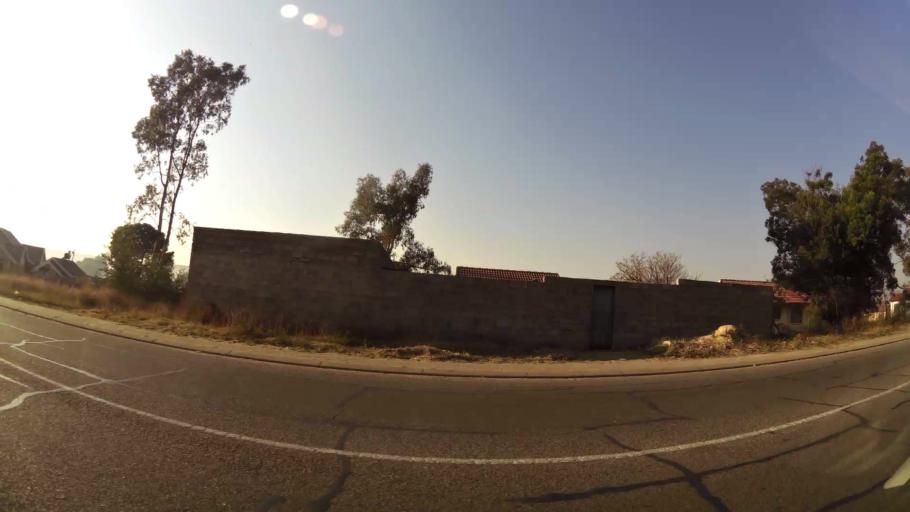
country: ZA
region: Gauteng
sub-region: City of Johannesburg Metropolitan Municipality
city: Modderfontein
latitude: -26.0900
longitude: 28.1021
